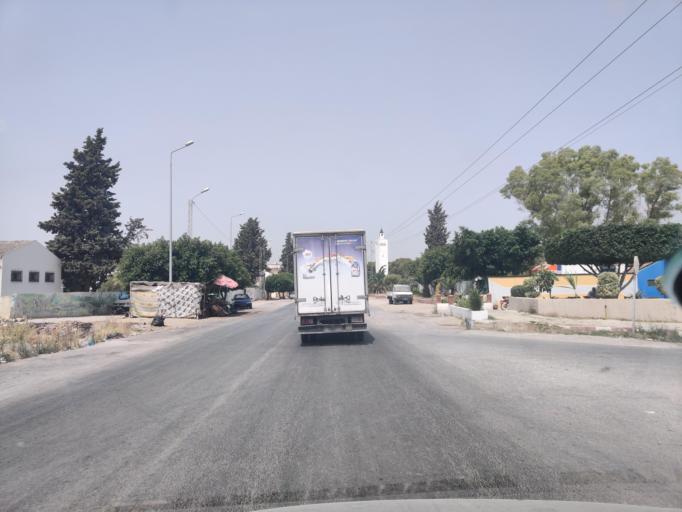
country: TN
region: Tunis
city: La Sebala du Mornag
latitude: 36.6611
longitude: 10.3258
